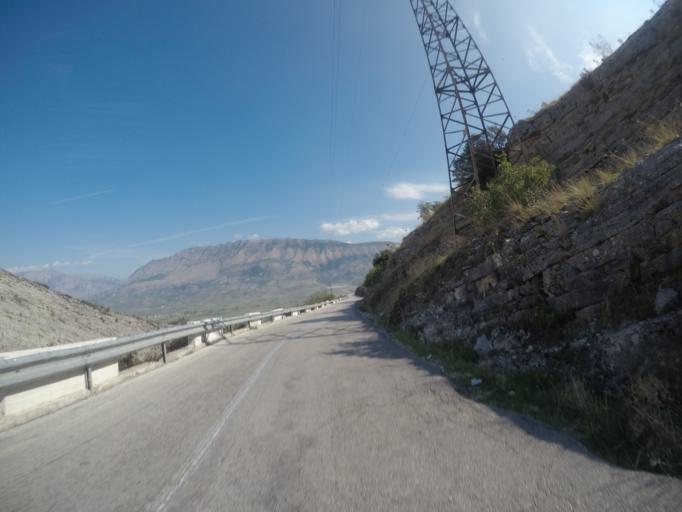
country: AL
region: Gjirokaster
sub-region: Rrethi i Gjirokastres
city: Libohove
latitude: 39.9464
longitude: 20.2391
